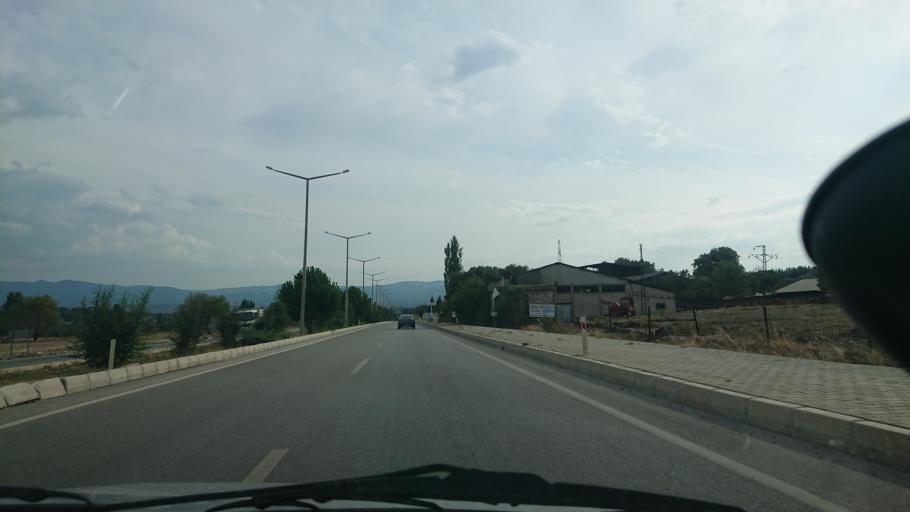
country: TR
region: Kuetahya
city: Gediz
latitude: 39.0048
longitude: 29.4052
